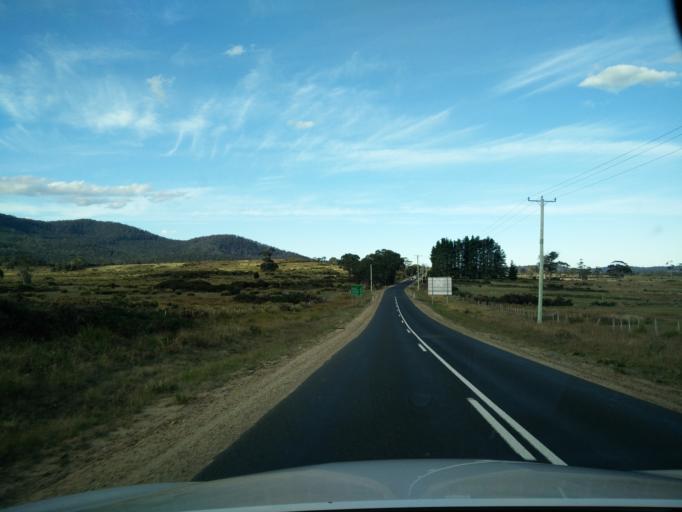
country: AU
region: Tasmania
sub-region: Break O'Day
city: St Helens
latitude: -41.9382
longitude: 148.2214
